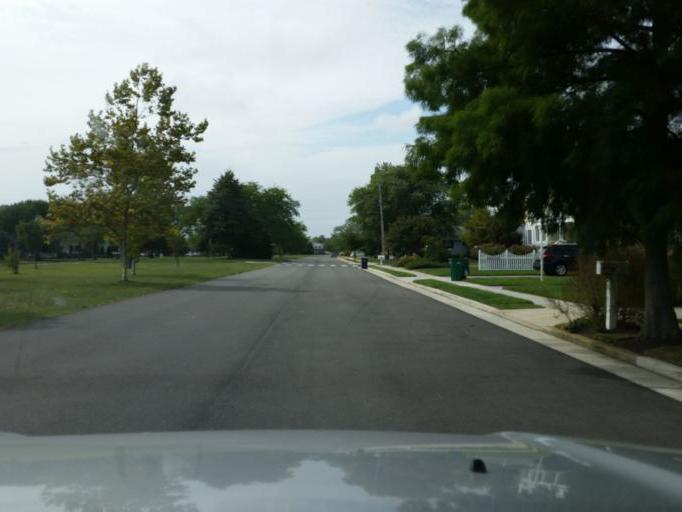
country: US
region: New Jersey
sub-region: Cape May County
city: Cape May
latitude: 38.9376
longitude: -74.9091
